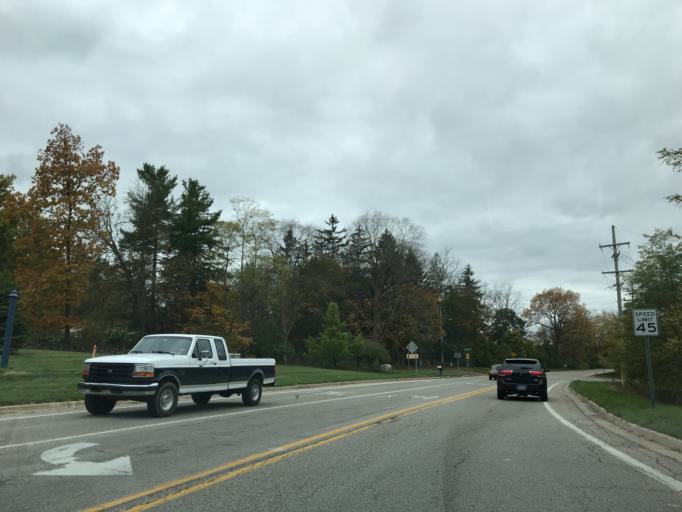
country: US
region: Michigan
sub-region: Washtenaw County
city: Ypsilanti
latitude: 42.2684
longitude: -83.6699
